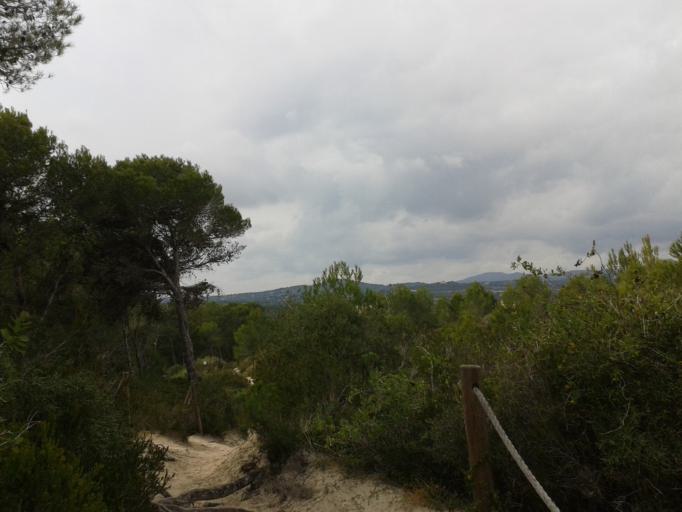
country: ES
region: Balearic Islands
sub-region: Illes Balears
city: Son Servera
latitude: 39.5830
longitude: 3.3854
